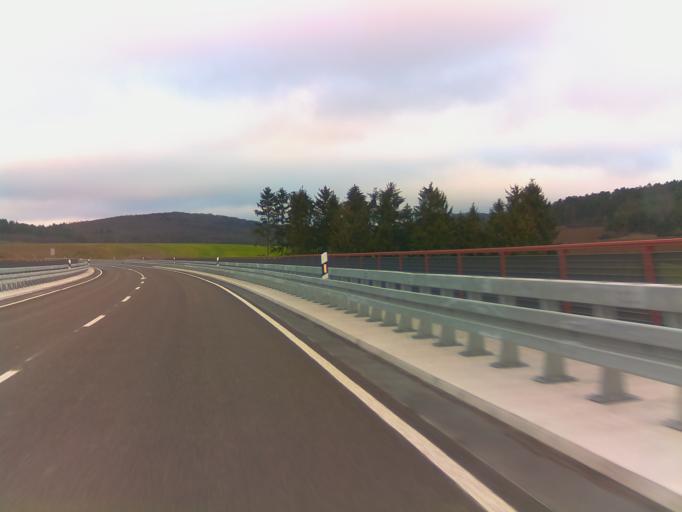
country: DE
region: Thuringia
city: Stadtilm
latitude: 50.7609
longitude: 11.0498
